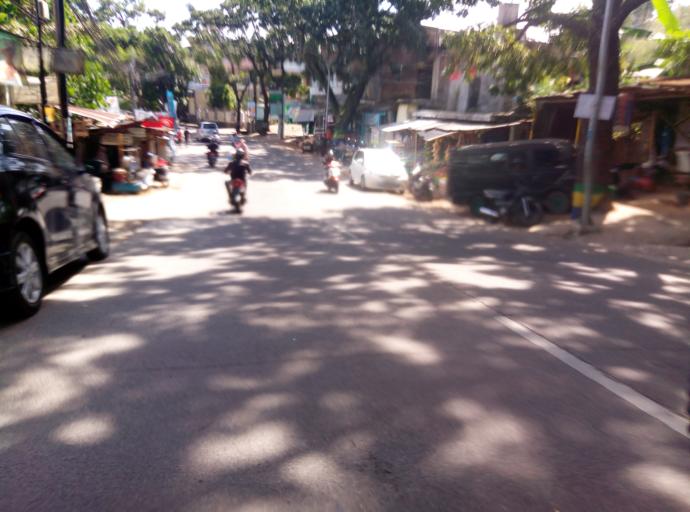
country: ID
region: West Java
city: Bandung
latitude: -6.8853
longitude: 107.6220
